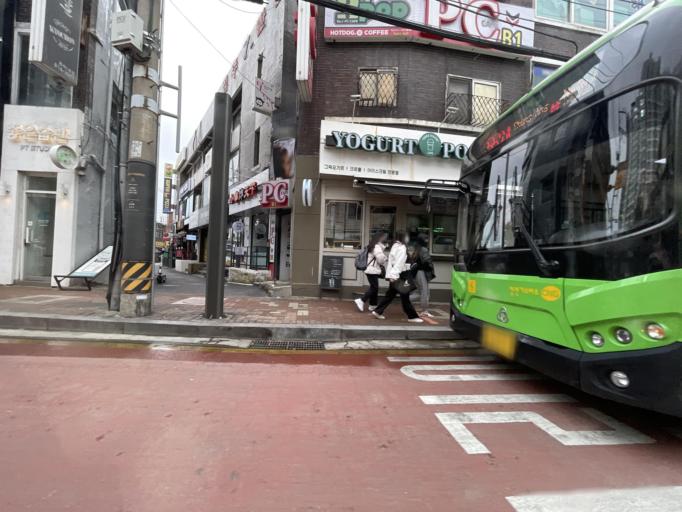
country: KR
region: Seoul
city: Seoul
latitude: 37.5086
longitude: 126.9616
